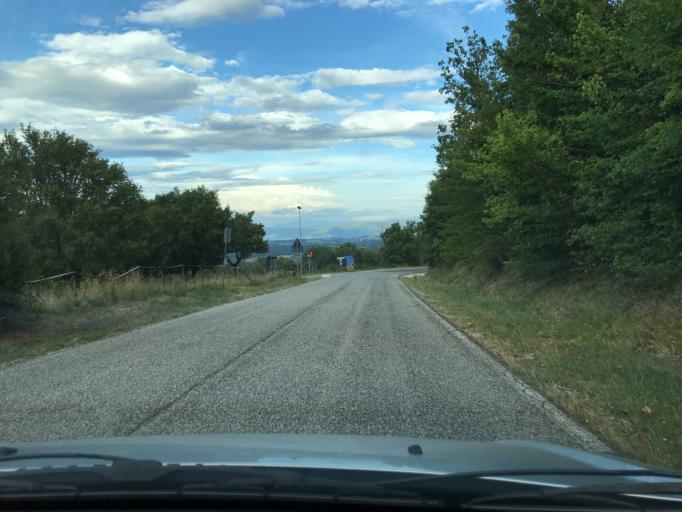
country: IT
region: Umbria
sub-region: Provincia di Terni
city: Guardea
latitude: 42.6560
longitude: 12.3469
